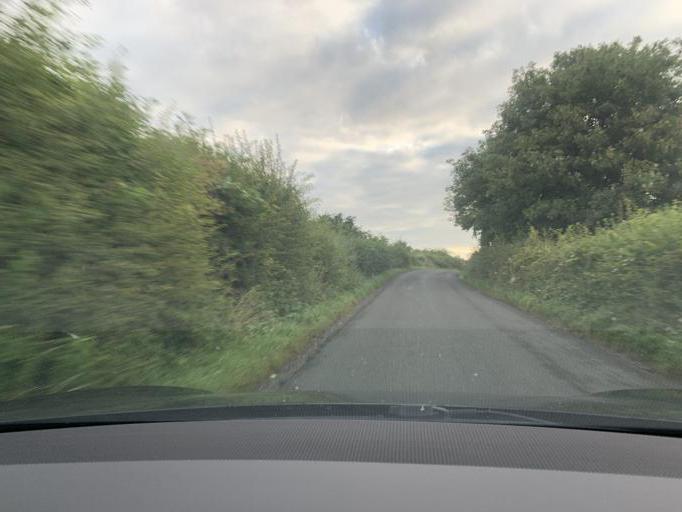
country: GB
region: England
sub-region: Wiltshire
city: Collingbourne Kingston
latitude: 51.2689
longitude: -1.6437
